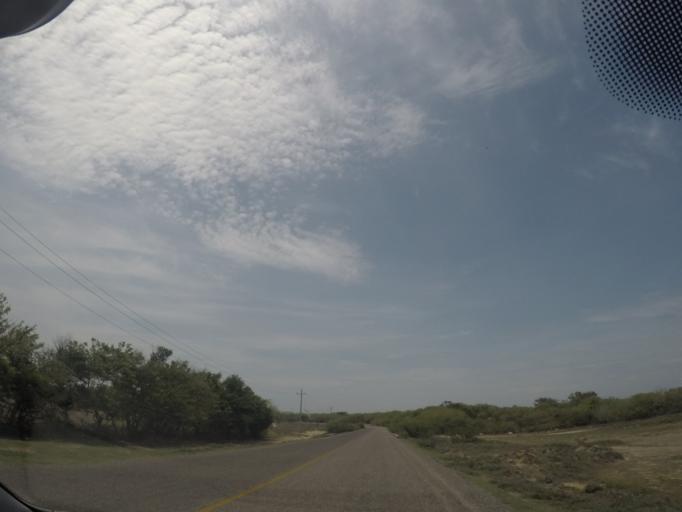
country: MX
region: Oaxaca
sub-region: San Mateo del Mar
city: Colonia Juarez
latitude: 16.2112
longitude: -95.0472
